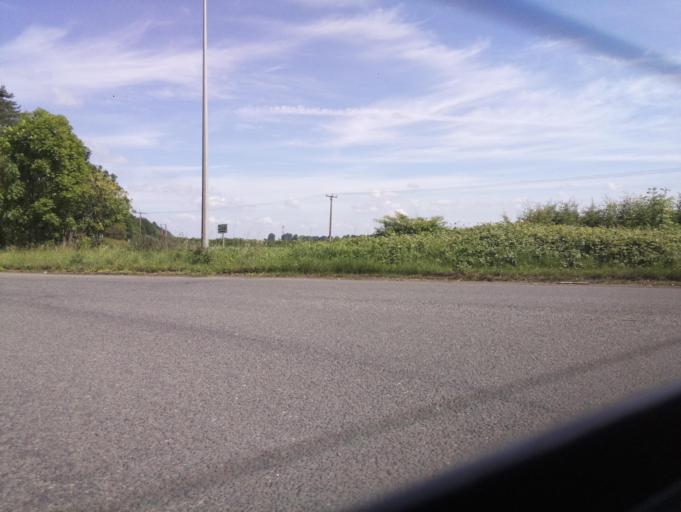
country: GB
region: England
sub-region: North Lincolnshire
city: Scawby
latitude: 53.5484
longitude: -0.5564
